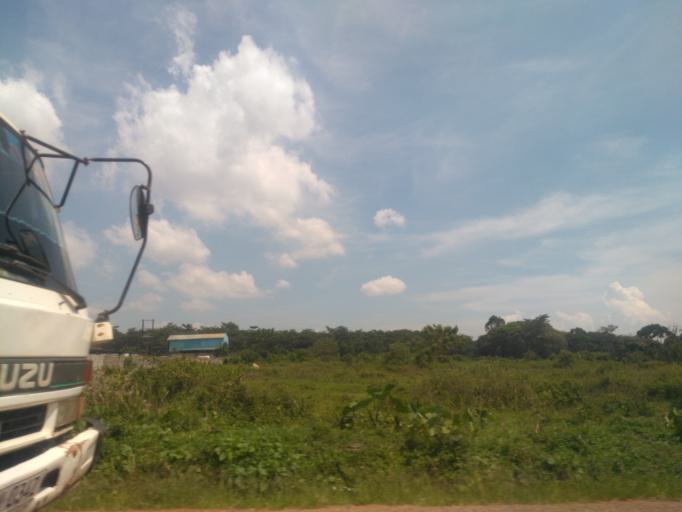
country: UG
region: Central Region
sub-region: Wakiso District
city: Entebbe
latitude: 0.0740
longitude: 32.4819
